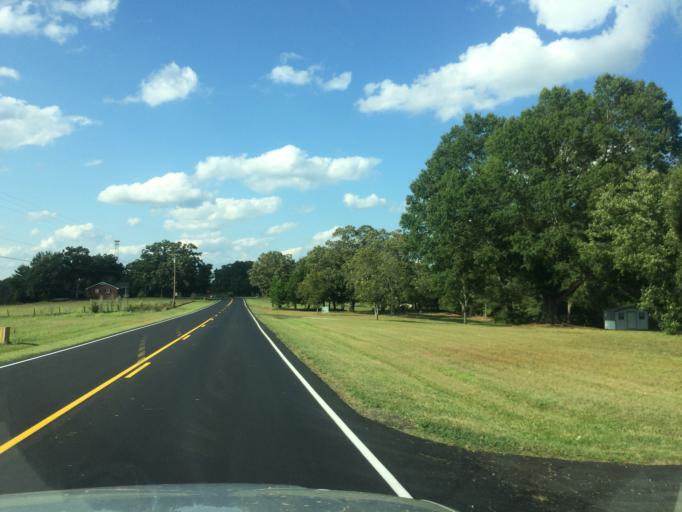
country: US
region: South Carolina
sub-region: Greenwood County
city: Ware Shoals
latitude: 34.4973
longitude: -82.1792
